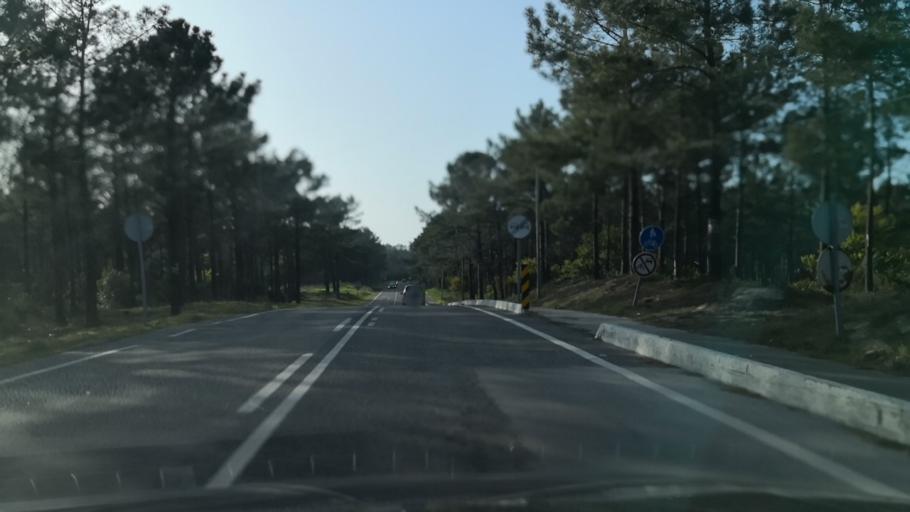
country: PT
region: Leiria
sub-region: Marinha Grande
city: Marinha Grande
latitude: 39.7511
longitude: -9.0150
